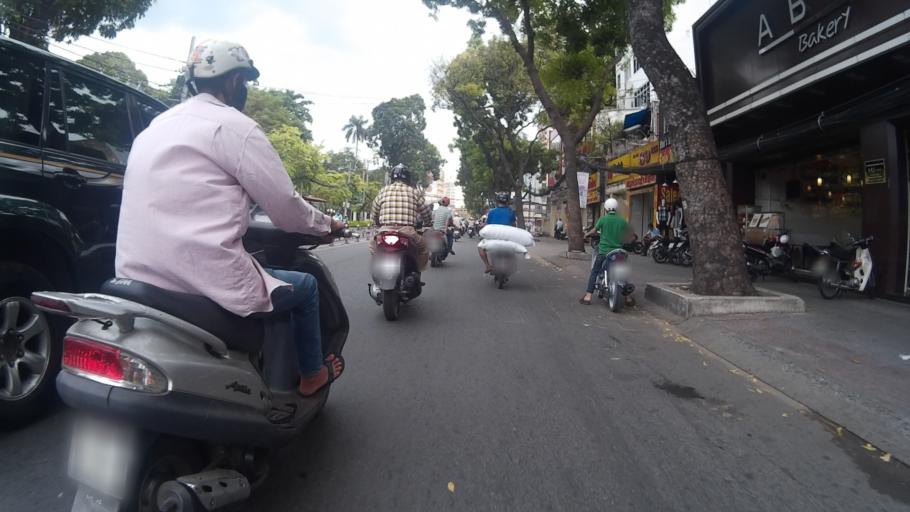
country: VN
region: Ho Chi Minh City
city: Quan Ba
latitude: 10.7730
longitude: 106.6902
